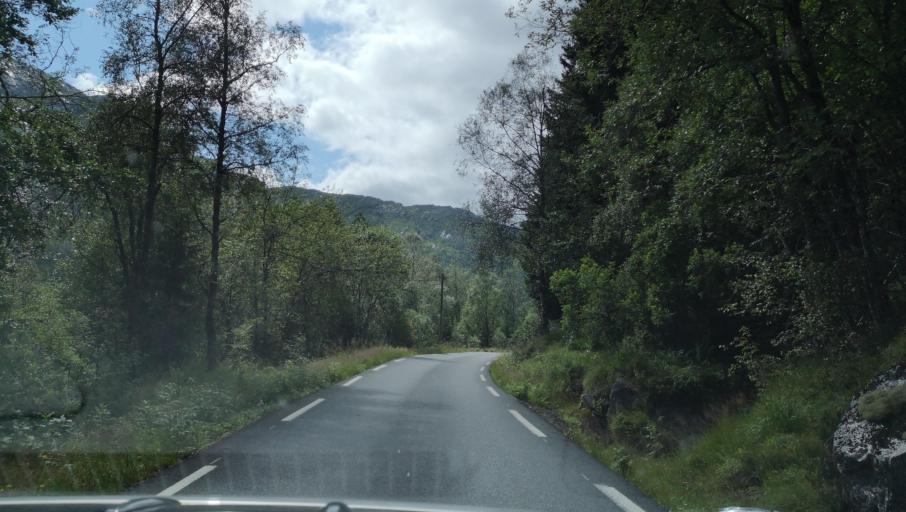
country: NO
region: Hordaland
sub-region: Modalen
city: Mo
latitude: 60.7865
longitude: 5.9357
